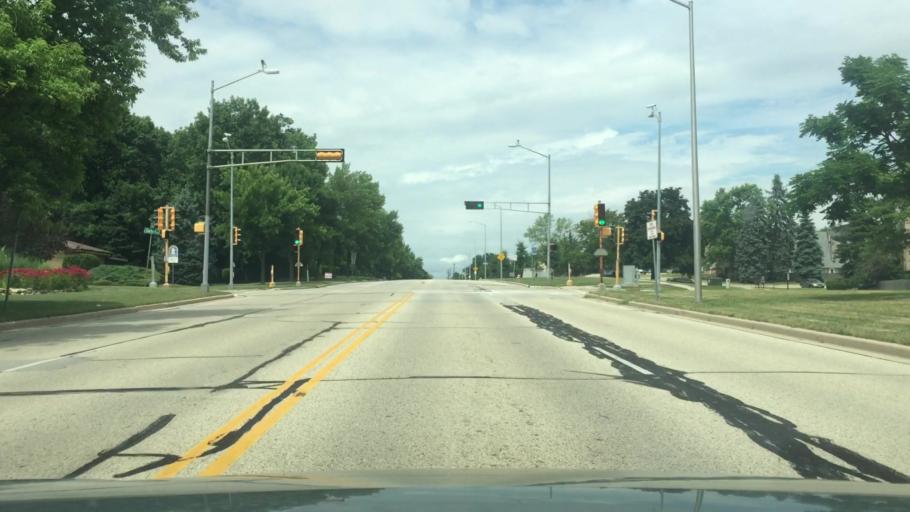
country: US
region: Wisconsin
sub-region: Waukesha County
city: Waukesha
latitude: 42.9840
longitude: -88.2273
